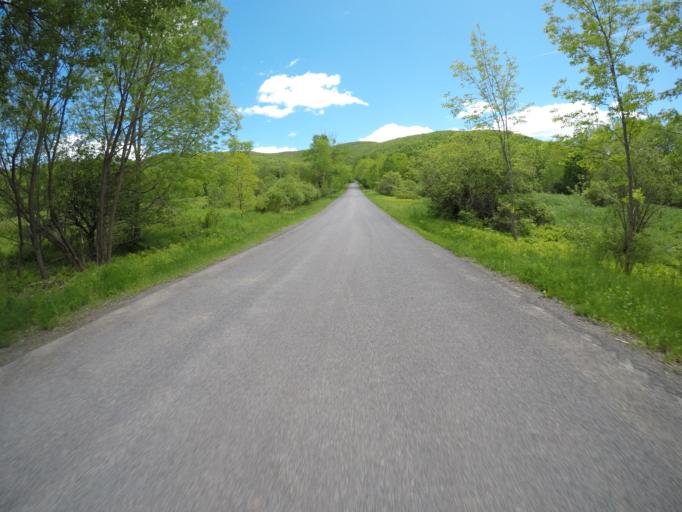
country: US
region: New York
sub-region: Delaware County
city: Stamford
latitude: 42.2797
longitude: -74.5094
